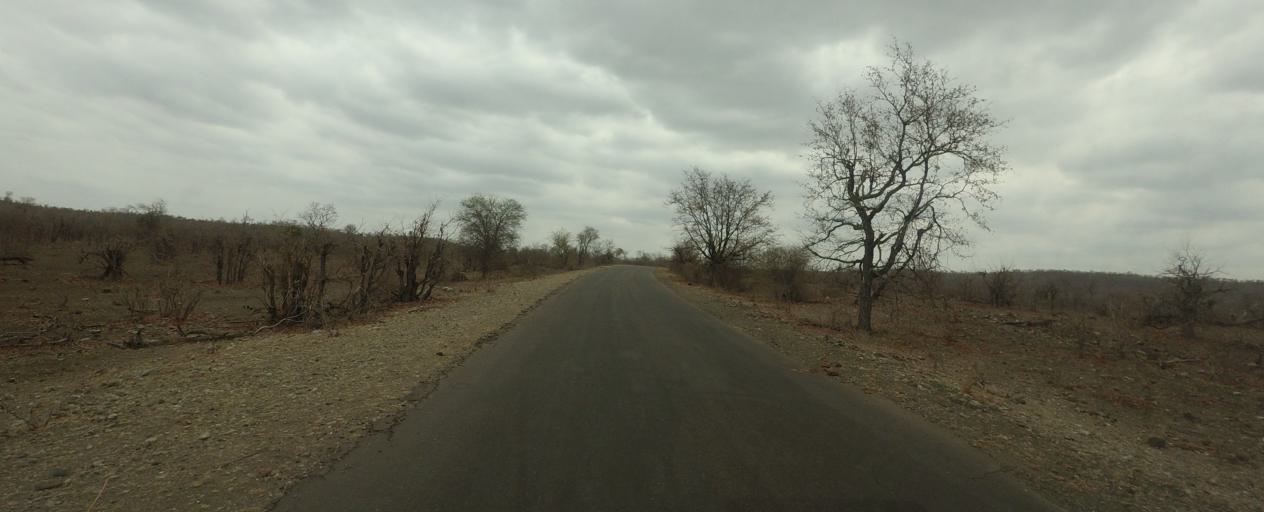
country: ZA
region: Limpopo
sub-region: Vhembe District Municipality
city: Mutale
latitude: -22.4054
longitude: 31.2093
